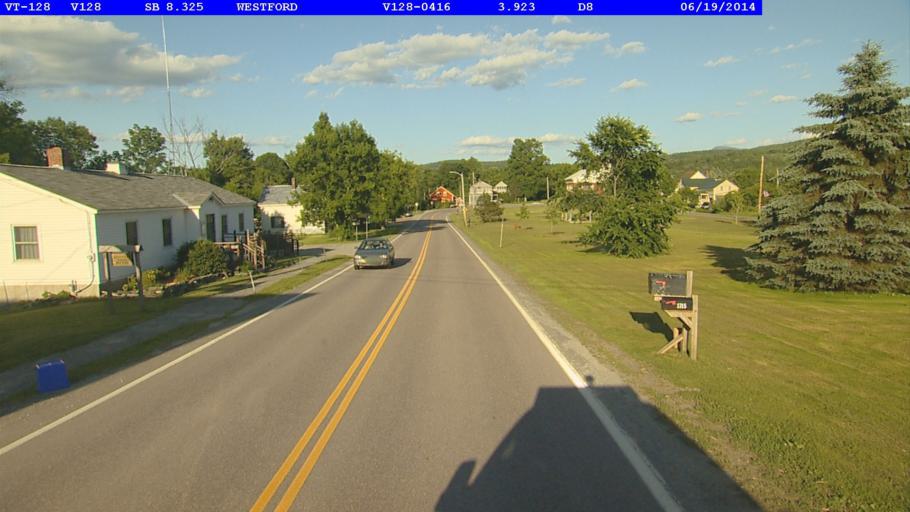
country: US
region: Vermont
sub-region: Chittenden County
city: Milton
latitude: 44.6120
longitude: -73.0113
